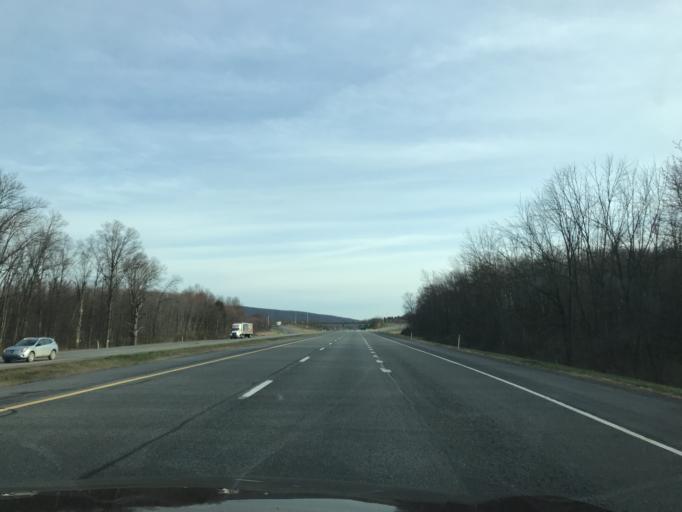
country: US
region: Pennsylvania
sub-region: Northumberland County
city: Milton
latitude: 40.9893
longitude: -76.8378
